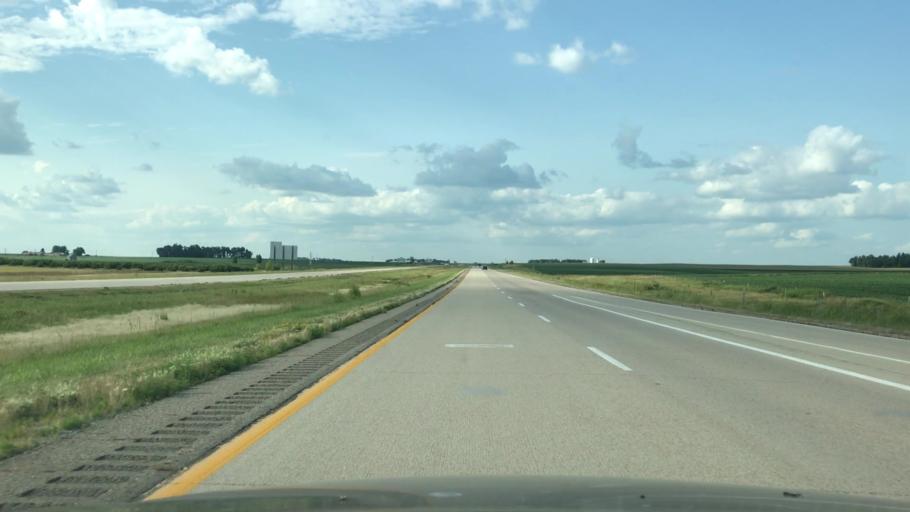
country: US
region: Iowa
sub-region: Osceola County
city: Sibley
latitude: 43.4371
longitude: -95.7133
